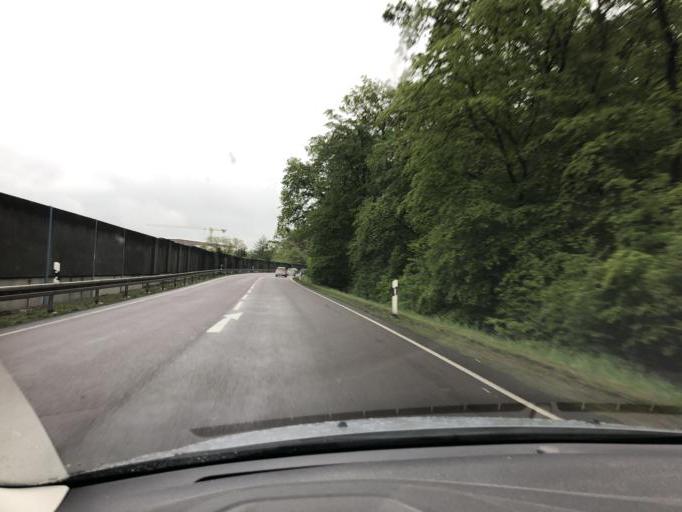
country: DE
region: Saxony-Anhalt
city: Dessau
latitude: 51.8039
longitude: 12.2269
